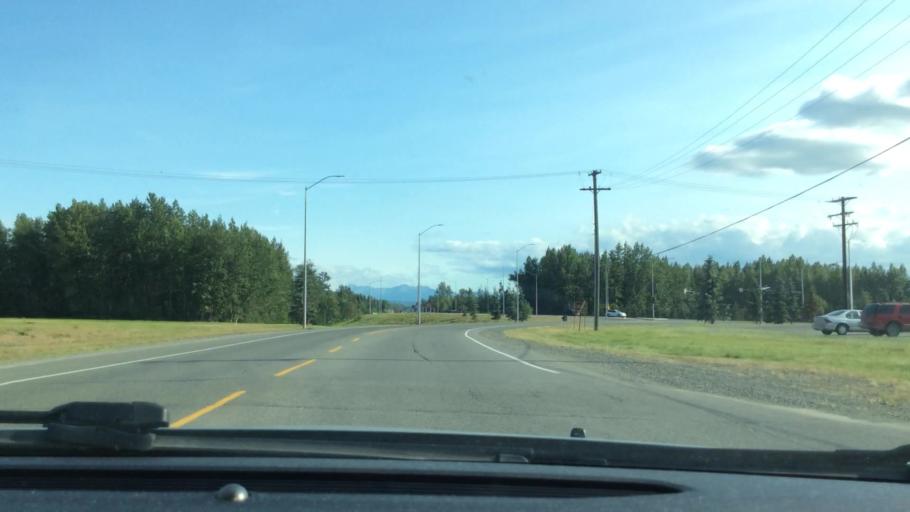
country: US
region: Alaska
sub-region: Anchorage Municipality
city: Anchorage
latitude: 61.2421
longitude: -149.7786
